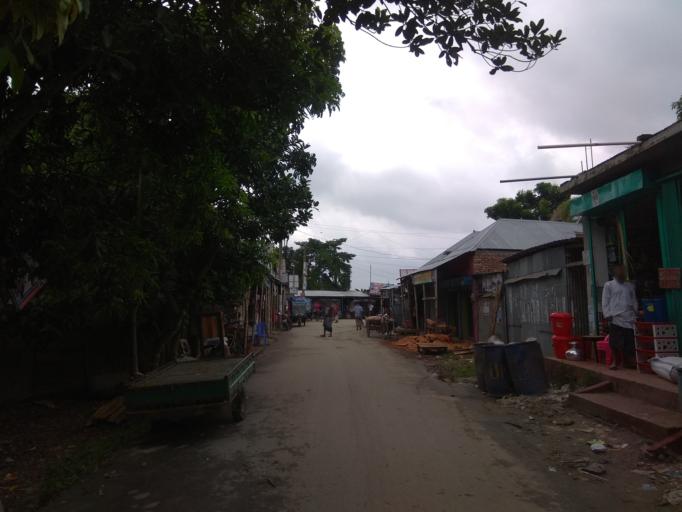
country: BD
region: Dhaka
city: Char Bhadrasan
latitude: 23.4170
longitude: 90.0708
